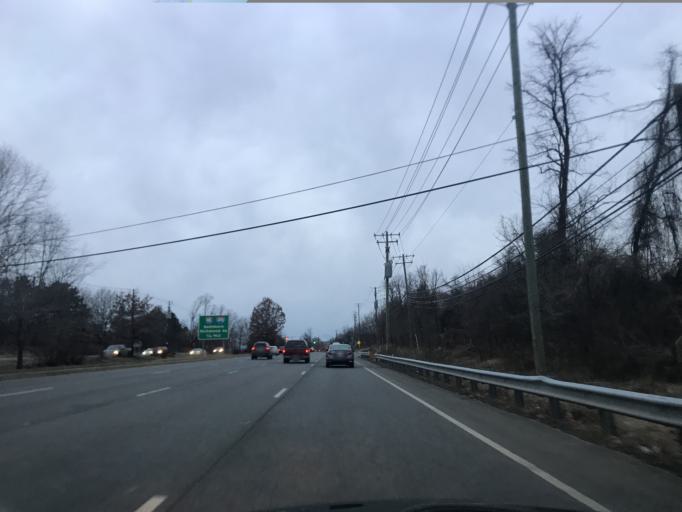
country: US
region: Maryland
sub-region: Prince George's County
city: Lake Arbor
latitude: 38.9148
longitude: -76.8420
